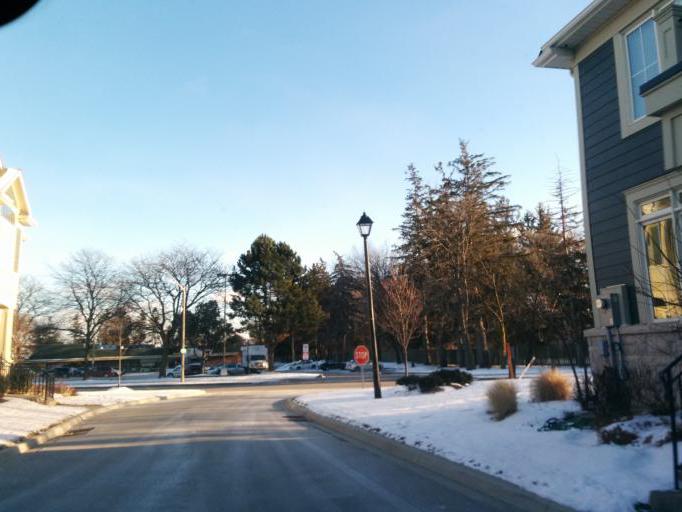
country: CA
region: Ontario
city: Mississauga
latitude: 43.5315
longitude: -79.6174
